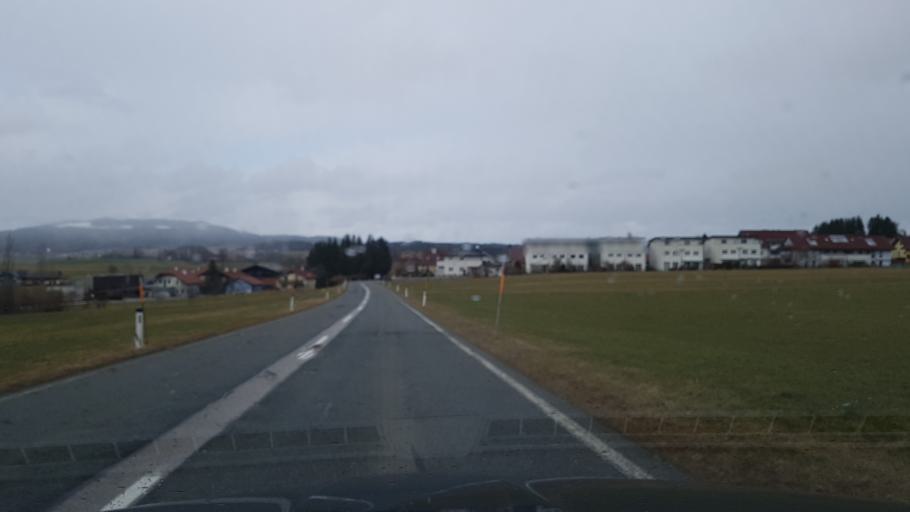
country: AT
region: Salzburg
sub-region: Politischer Bezirk Salzburg-Umgebung
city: Neumarkt am Wallersee
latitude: 47.9295
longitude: 13.2210
